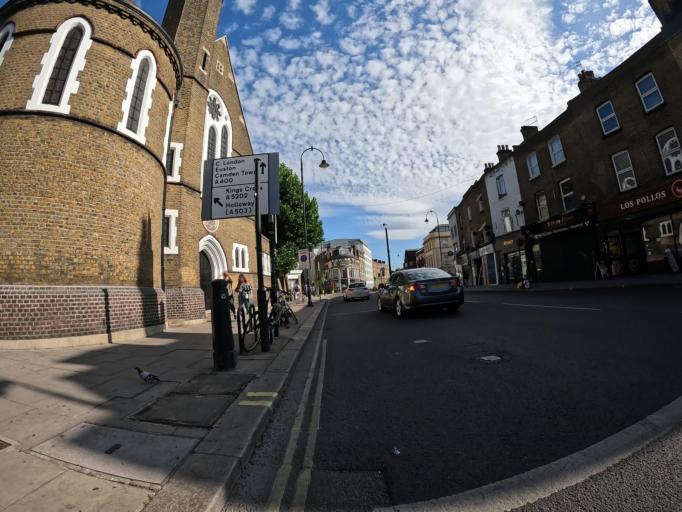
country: GB
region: England
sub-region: Greater London
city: Camden Town
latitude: 51.5458
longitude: -0.1416
